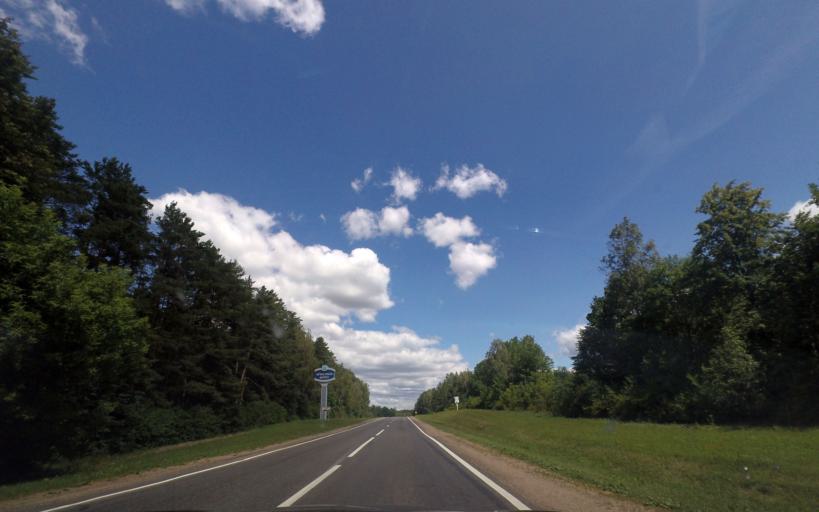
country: BY
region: Grodnenskaya
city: Hrodna
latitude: 53.7596
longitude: 23.8283
